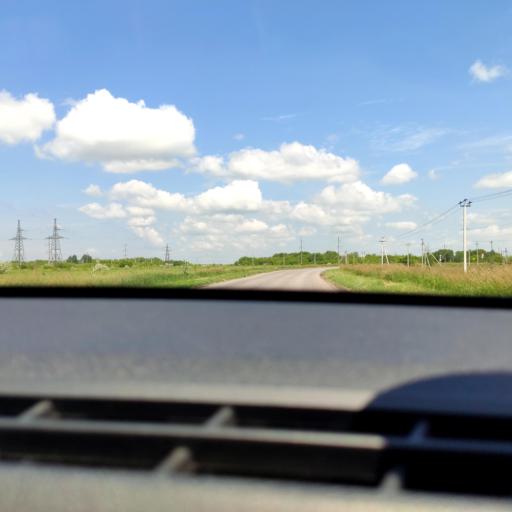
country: RU
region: Samara
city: Podstepki
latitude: 53.5632
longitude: 49.0927
